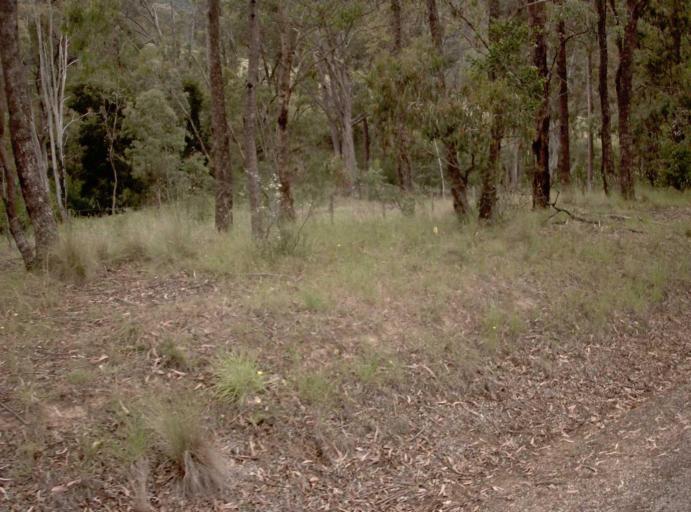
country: AU
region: Victoria
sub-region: East Gippsland
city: Bairnsdale
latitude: -37.5516
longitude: 147.1986
